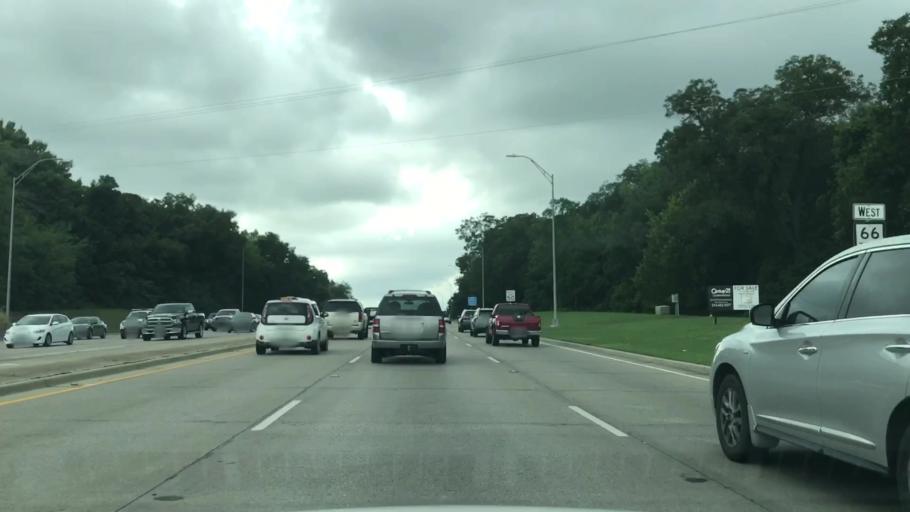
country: US
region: Texas
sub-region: Dallas County
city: Rowlett
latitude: 32.9103
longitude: -96.5993
